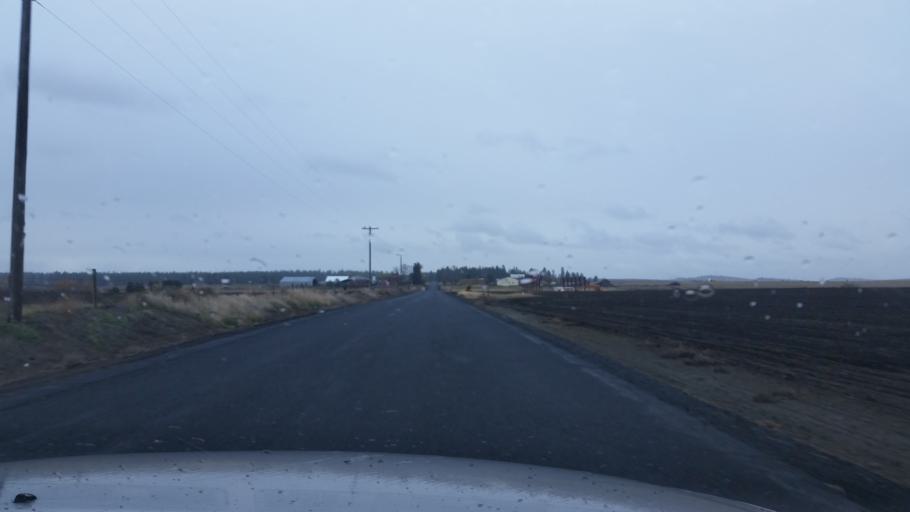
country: US
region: Washington
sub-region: Spokane County
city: Medical Lake
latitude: 47.6144
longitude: -117.7541
